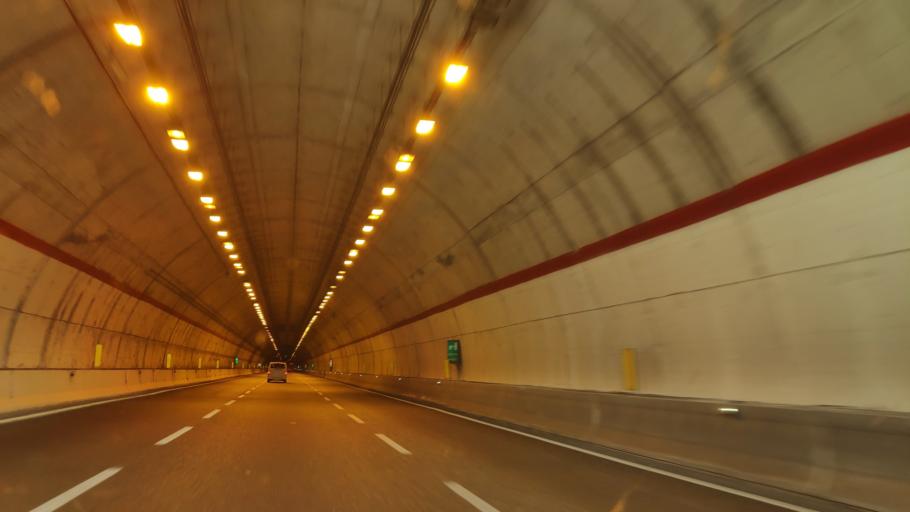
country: IT
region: Campania
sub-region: Provincia di Salerno
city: Contursi Terme
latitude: 40.6194
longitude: 15.2439
